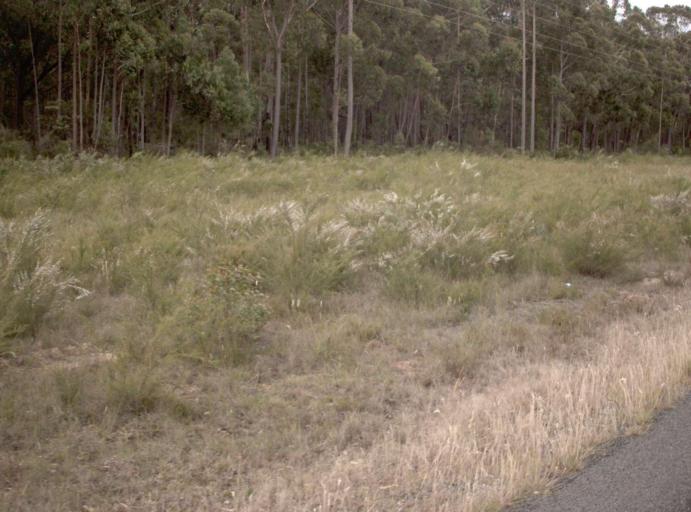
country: AU
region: Victoria
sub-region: East Gippsland
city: Lakes Entrance
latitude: -37.7293
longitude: 147.9461
